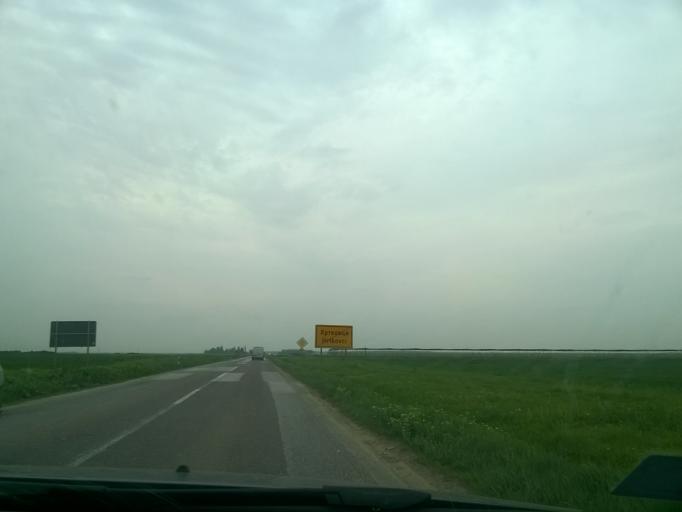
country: RS
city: Hrtkovci
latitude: 44.8675
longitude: 19.7710
